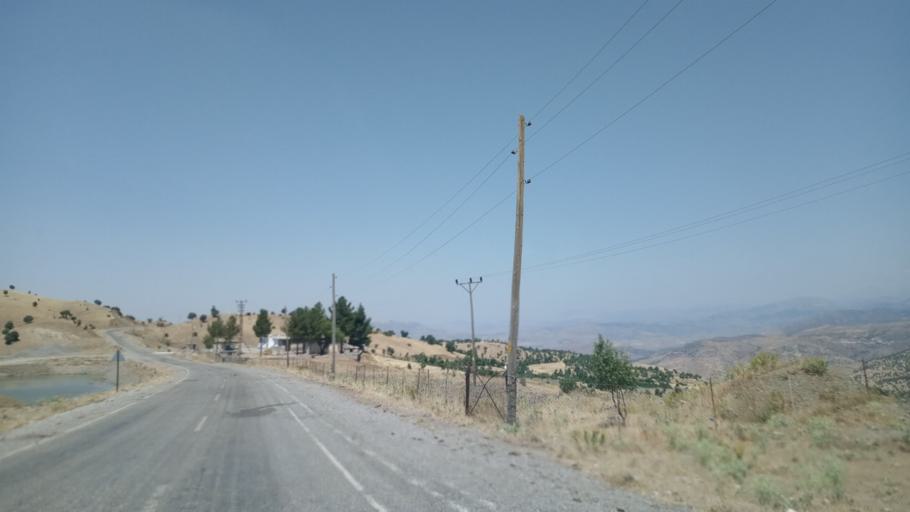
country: TR
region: Siirt
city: Dilektepe
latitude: 38.0765
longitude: 41.8248
